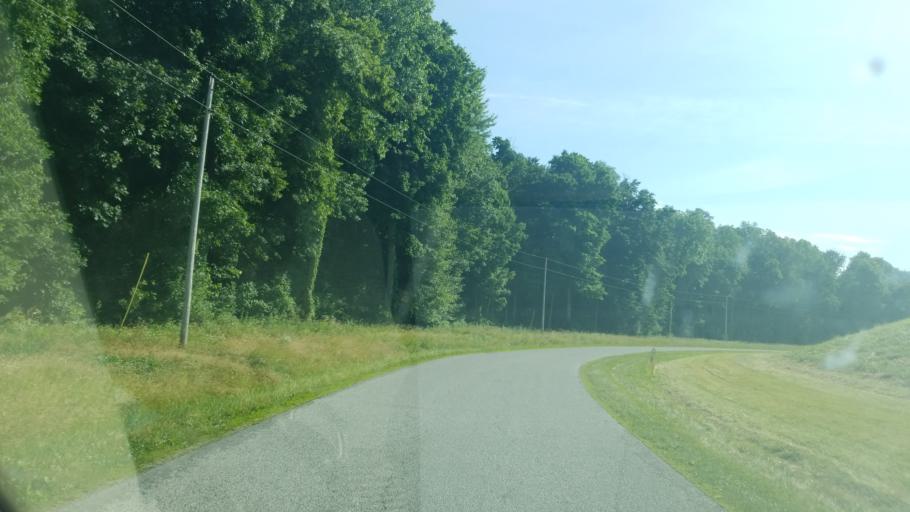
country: US
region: Ohio
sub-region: Hancock County
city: Findlay
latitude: 41.0283
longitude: -83.5805
